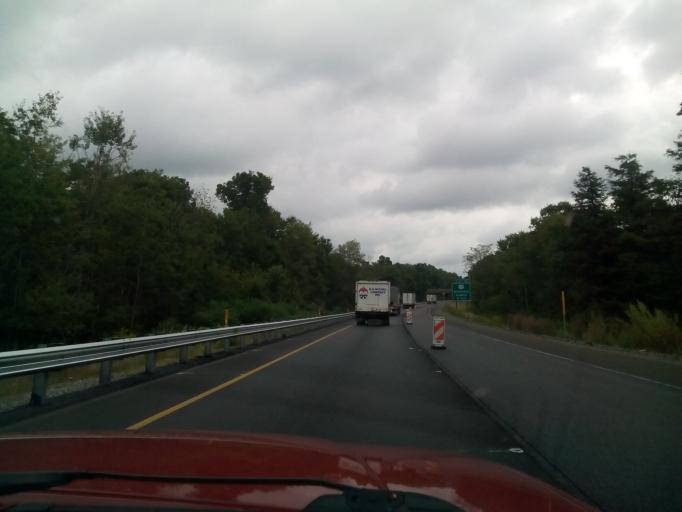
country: US
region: Pennsylvania
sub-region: Jefferson County
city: Falls Creek
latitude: 41.1579
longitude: -78.8286
